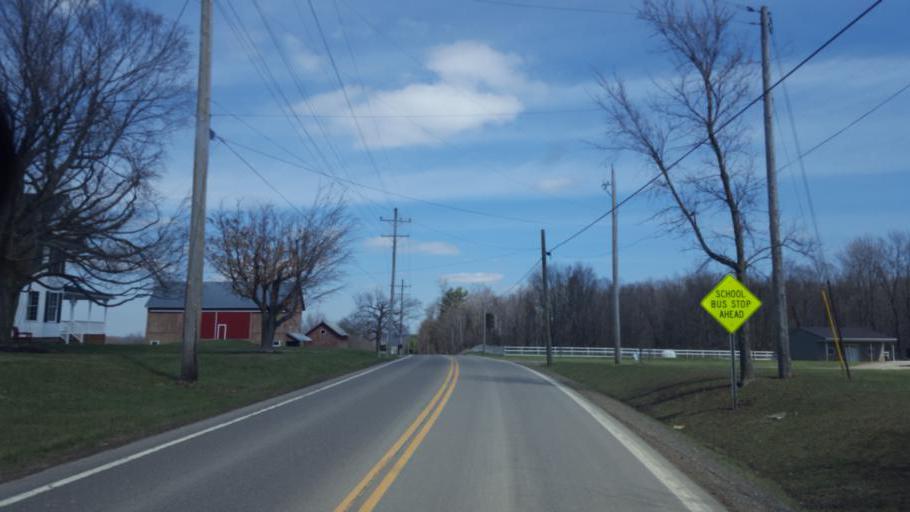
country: US
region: Ohio
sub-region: Richland County
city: Lincoln Heights
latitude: 40.8192
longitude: -82.4859
